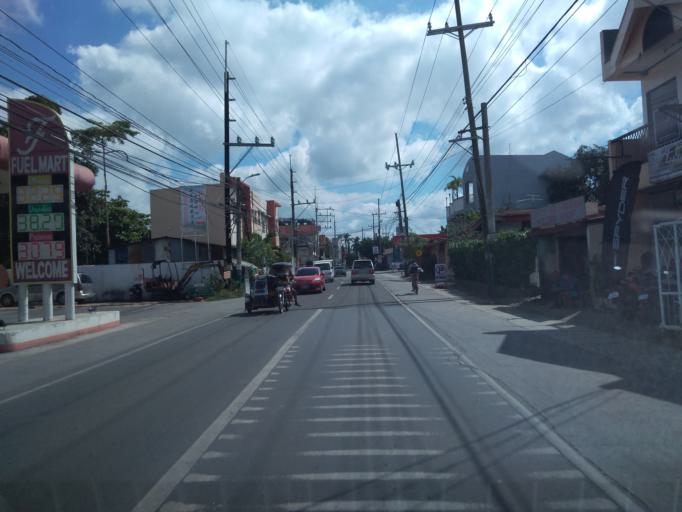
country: PH
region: Central Luzon
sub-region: Province of Bulacan
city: Santa Maria
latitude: 14.8175
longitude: 120.9555
